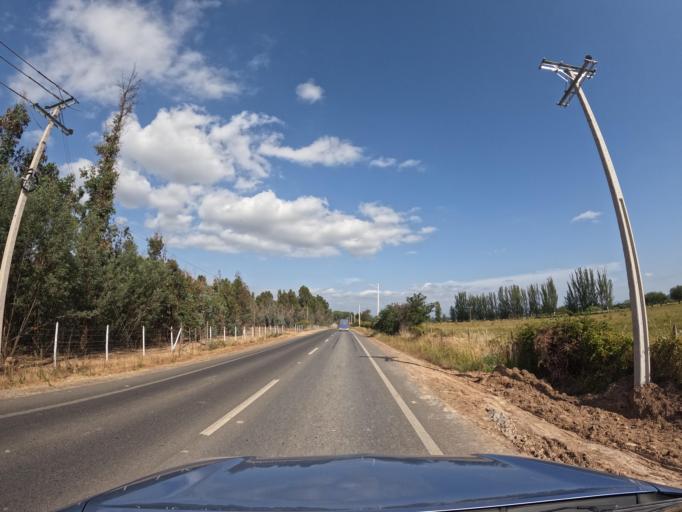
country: CL
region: Maule
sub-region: Provincia de Curico
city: Molina
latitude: -35.2571
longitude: -71.3398
